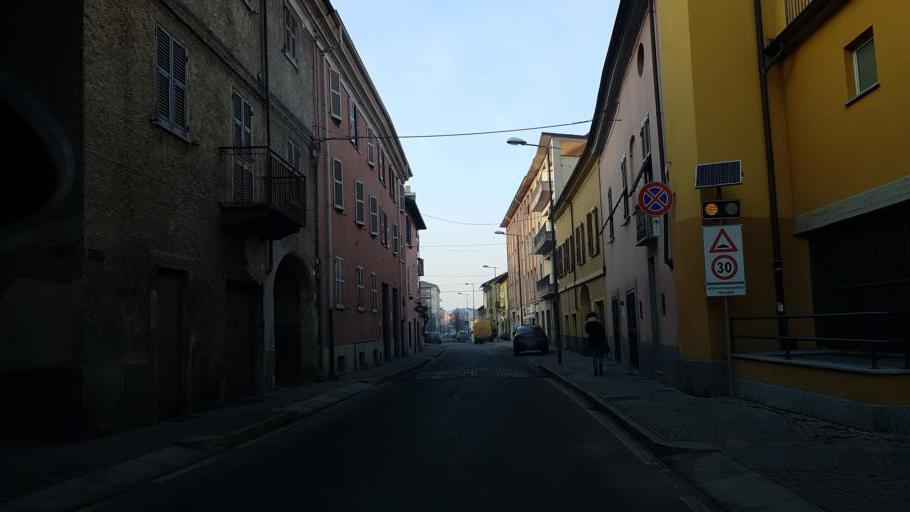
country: IT
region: Piedmont
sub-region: Provincia di Alessandria
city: Novi Ligure
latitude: 44.7614
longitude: 8.7808
